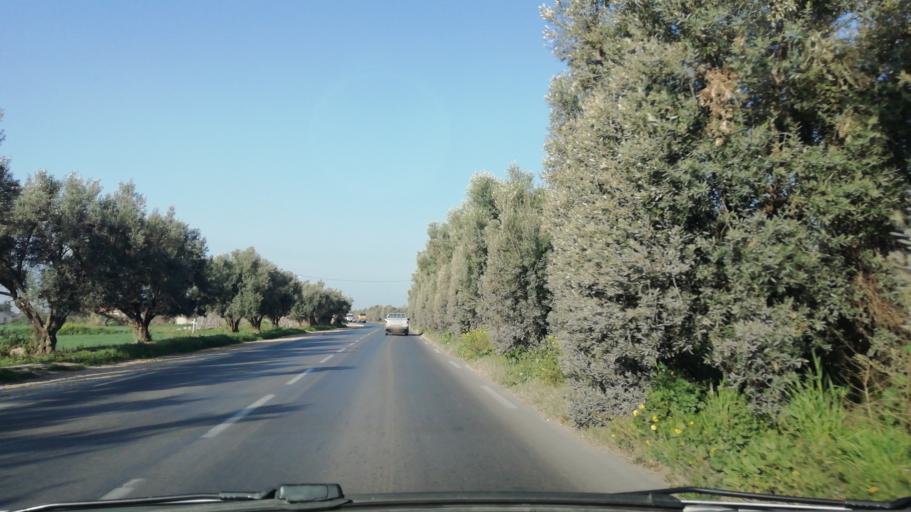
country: DZ
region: Mostaganem
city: Mostaganem
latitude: 35.7532
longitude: 0.1863
